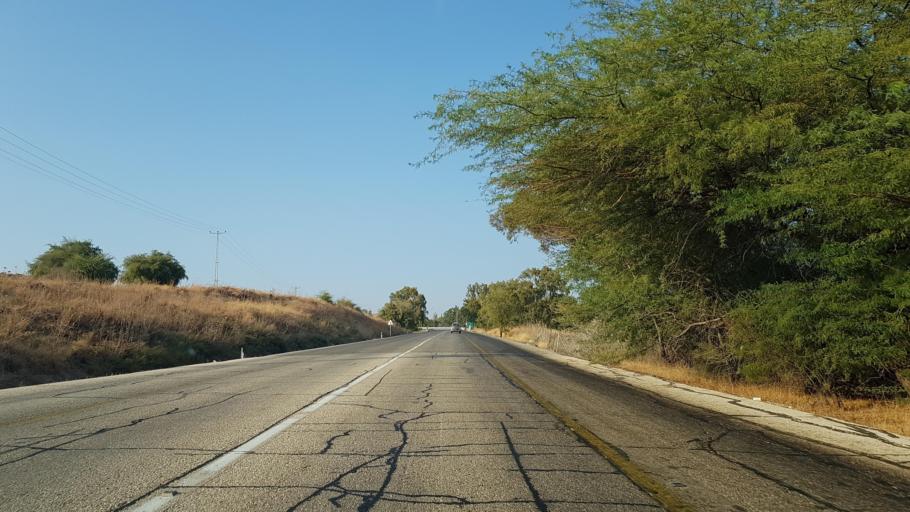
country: SY
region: Quneitra
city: Al Butayhah
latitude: 32.9077
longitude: 35.5972
